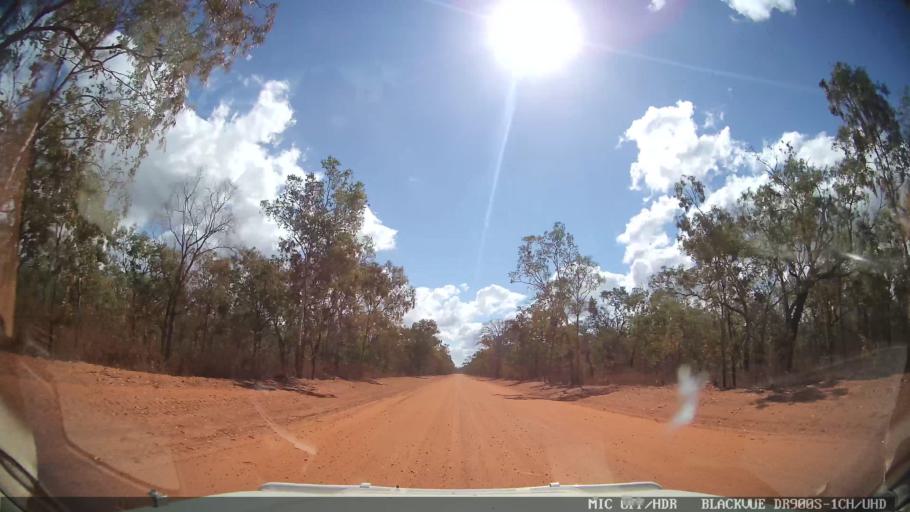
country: AU
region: Queensland
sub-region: Cook
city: Cooktown
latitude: -15.1971
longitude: 144.3825
